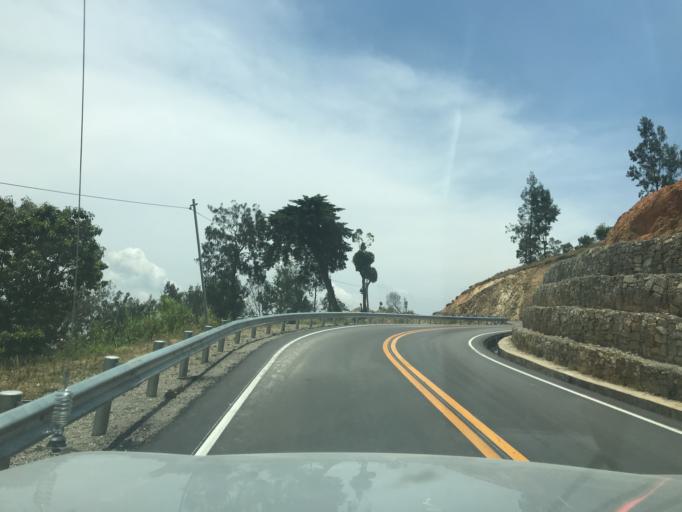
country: TL
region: Manufahi
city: Same
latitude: -8.8788
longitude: 125.5945
